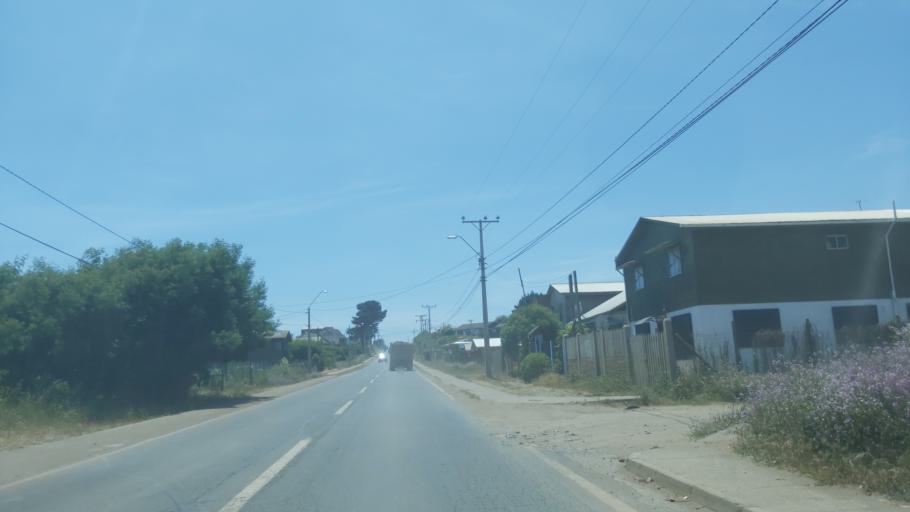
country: CL
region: Maule
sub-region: Provincia de Cauquenes
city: Cauquenes
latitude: -35.8063
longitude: -72.5685
